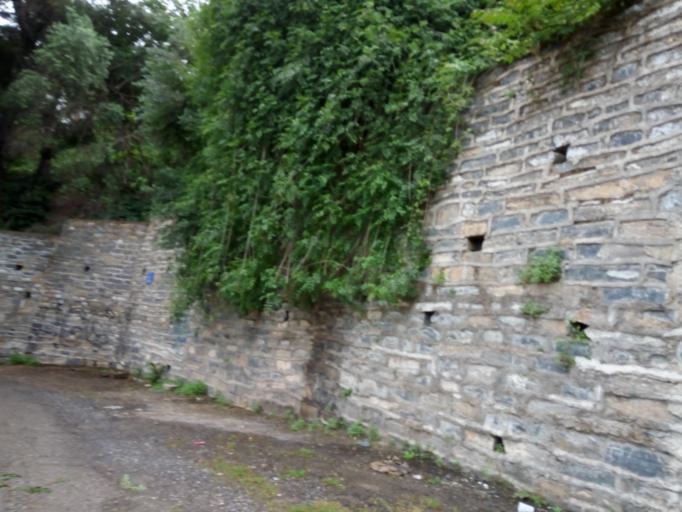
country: DZ
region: Alger
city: Algiers
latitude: 36.7638
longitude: 3.0407
